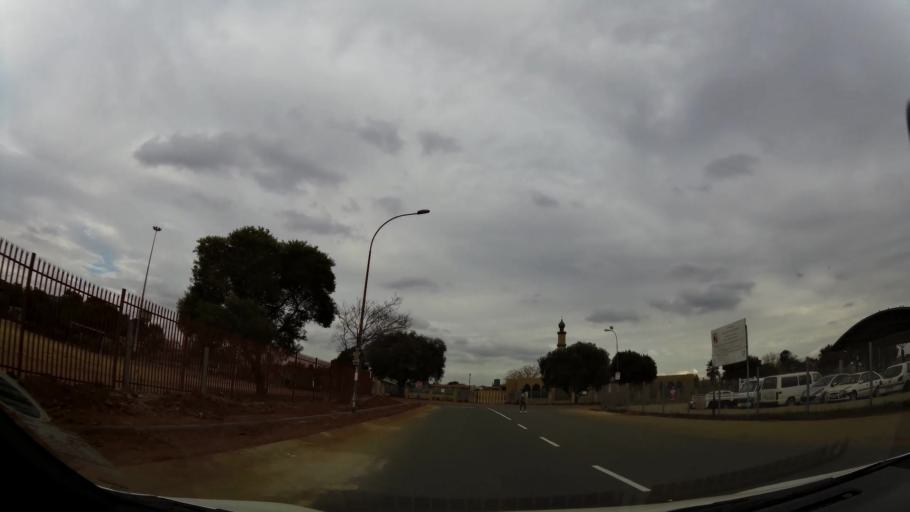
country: ZA
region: Gauteng
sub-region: Ekurhuleni Metropolitan Municipality
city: Germiston
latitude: -26.3887
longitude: 28.1443
